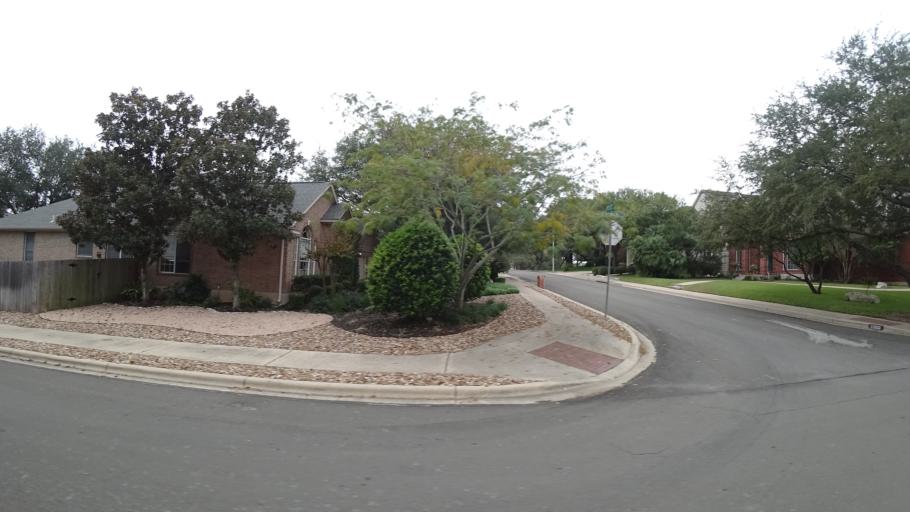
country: US
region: Texas
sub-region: Williamson County
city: Anderson Mill
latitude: 30.4325
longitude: -97.8266
